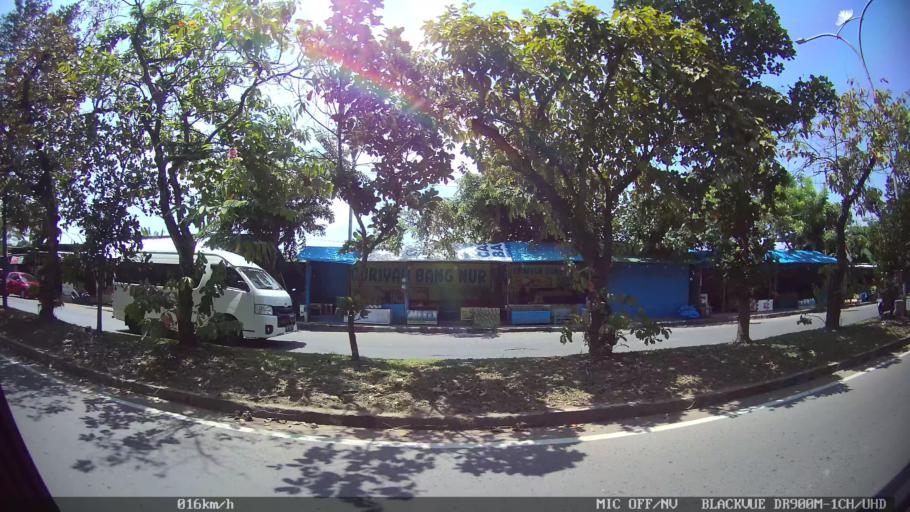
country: ID
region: Lampung
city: Kedaton
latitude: -5.3827
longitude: 105.2805
